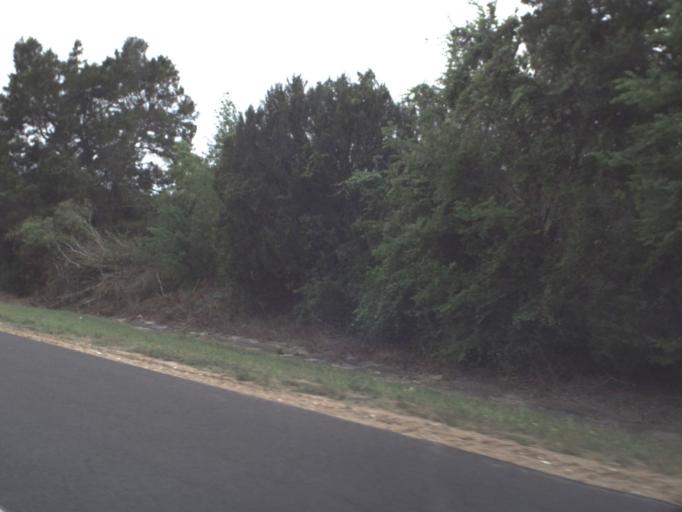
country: US
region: Florida
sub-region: Marion County
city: Citra
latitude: 29.3597
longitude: -82.2233
